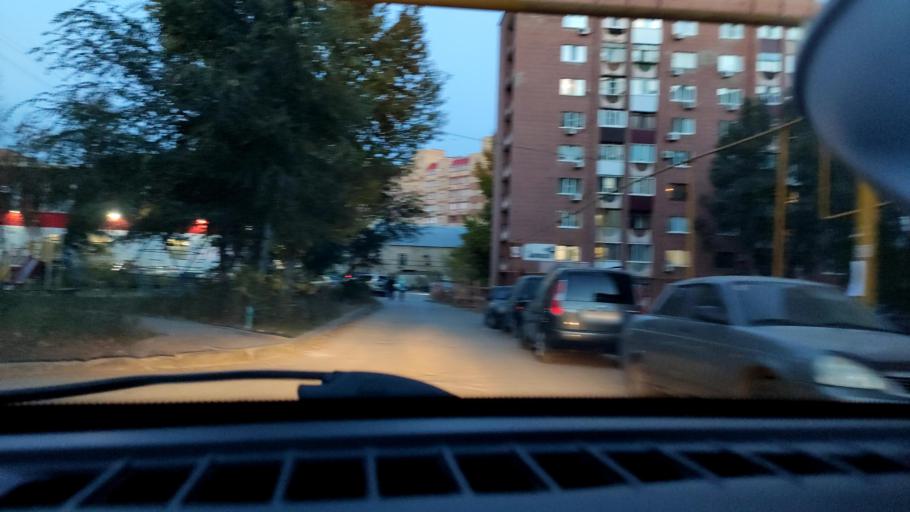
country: RU
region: Samara
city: Samara
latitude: 53.2040
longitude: 50.2232
